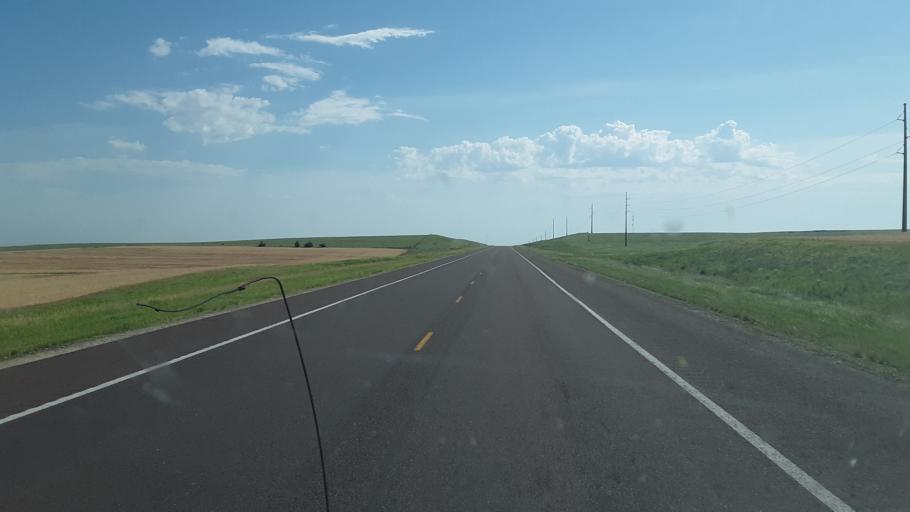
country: US
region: Kansas
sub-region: Ellsworth County
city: Ellsworth
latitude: 38.6467
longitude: -98.3303
